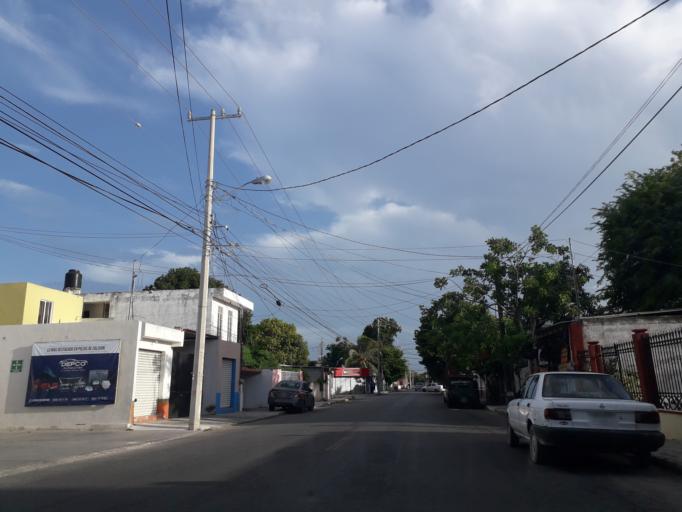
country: MX
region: Yucatan
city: Merida
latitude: 21.0200
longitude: -89.6317
